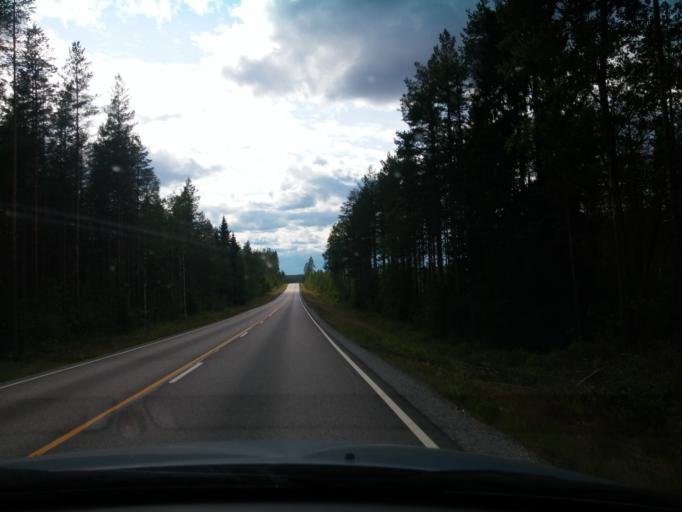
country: FI
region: Central Finland
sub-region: Saarijaervi-Viitasaari
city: Pylkoenmaeki
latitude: 62.6012
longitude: 24.6416
